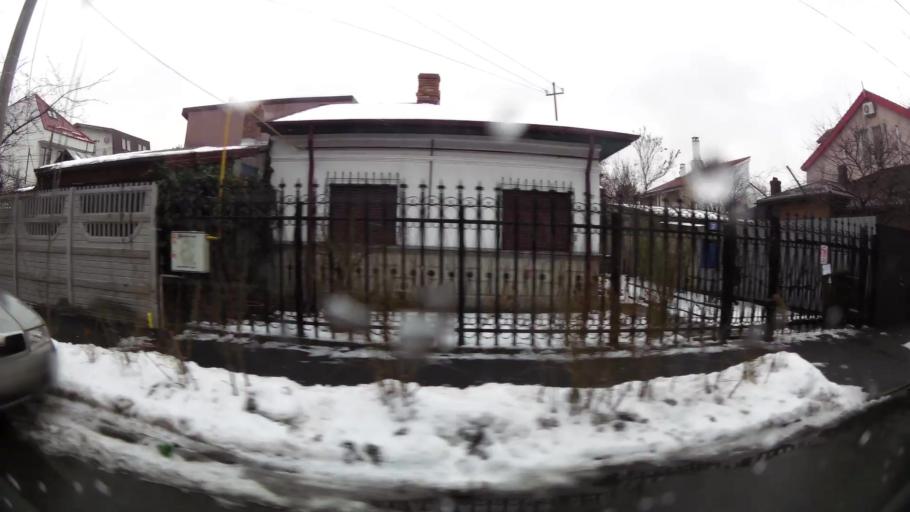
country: RO
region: Ilfov
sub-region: Comuna Chiajna
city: Rosu
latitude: 44.4924
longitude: 26.0358
